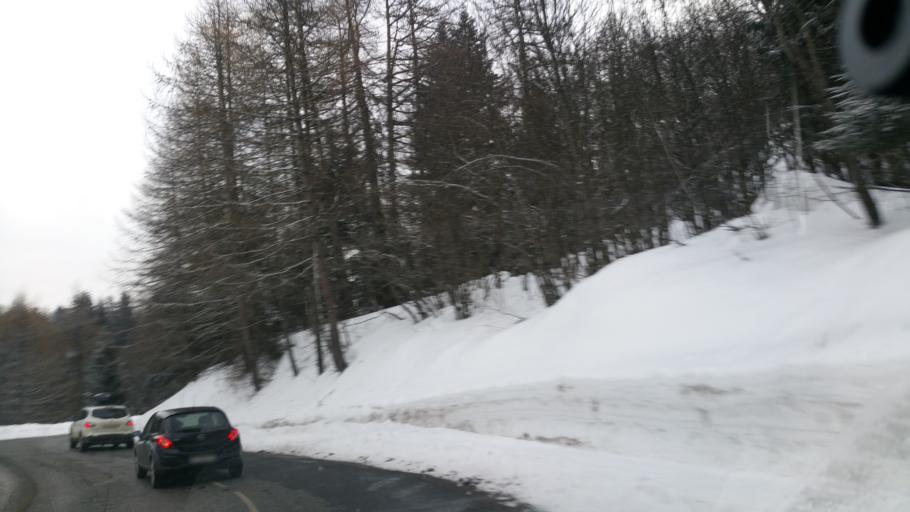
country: FR
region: Rhone-Alpes
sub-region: Departement de la Savoie
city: Villargondran
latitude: 45.2303
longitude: 6.4073
